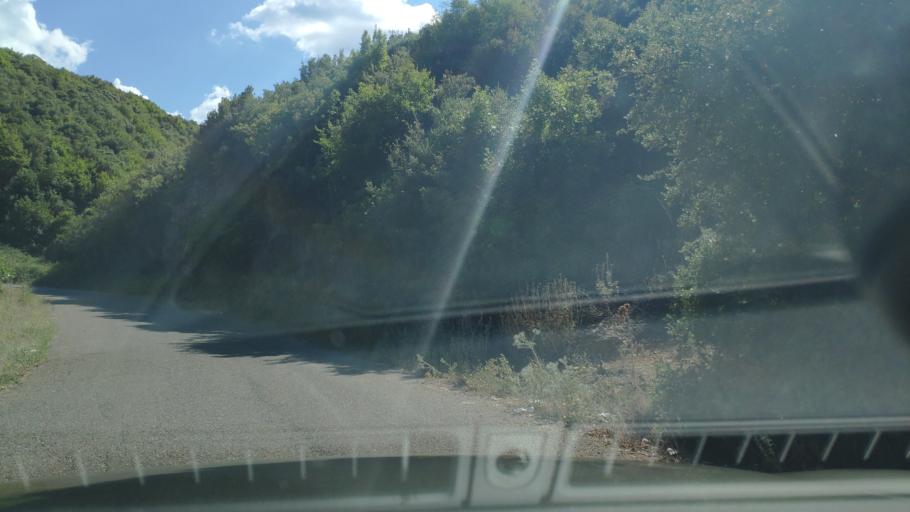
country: GR
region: West Greece
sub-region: Nomos Aitolias kai Akarnanias
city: Katouna
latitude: 38.8034
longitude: 21.1096
